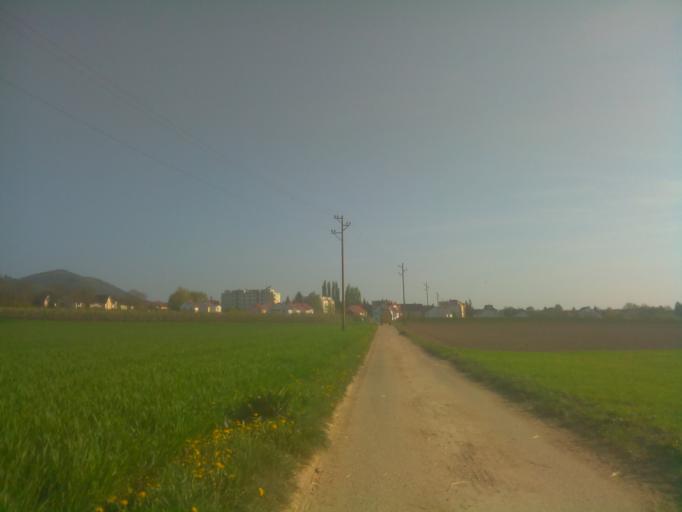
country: DE
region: Baden-Wuerttemberg
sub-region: Karlsruhe Region
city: Schriesheim
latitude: 49.5044
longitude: 8.6544
